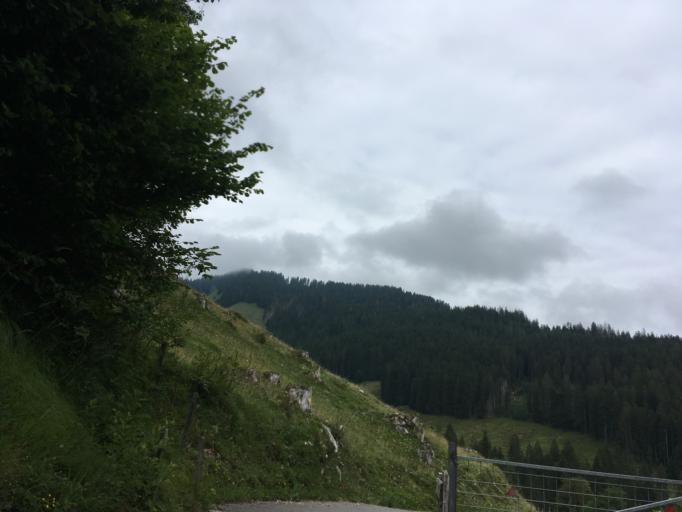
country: CH
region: Bern
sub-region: Interlaken-Oberhasli District
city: Beatenberg
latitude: 46.7077
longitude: 7.8081
